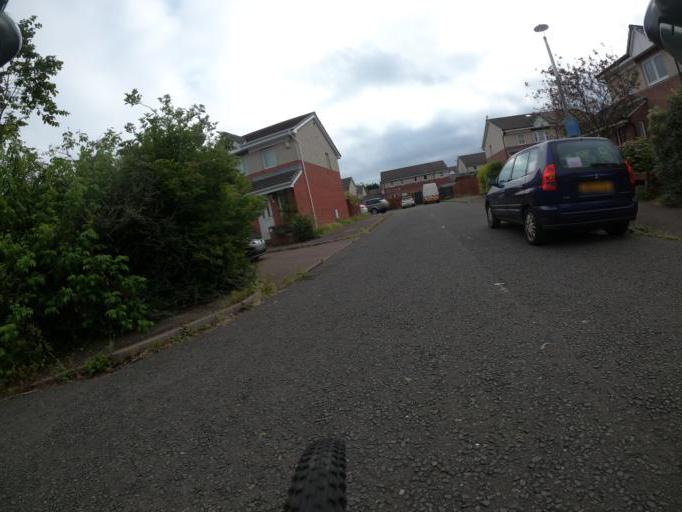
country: GB
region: Scotland
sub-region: Edinburgh
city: Edinburgh
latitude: 55.9745
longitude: -3.2484
